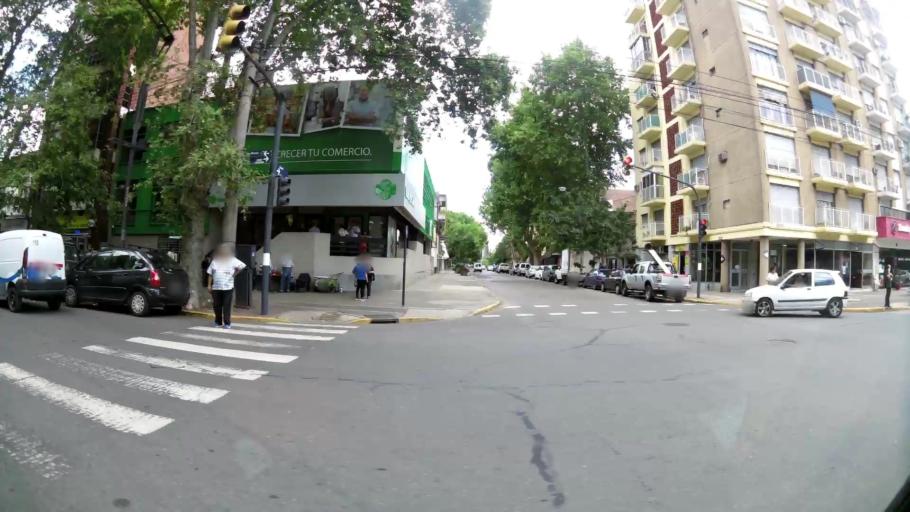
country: AR
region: Santa Fe
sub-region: Departamento de Rosario
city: Rosario
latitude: -32.9713
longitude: -60.6429
